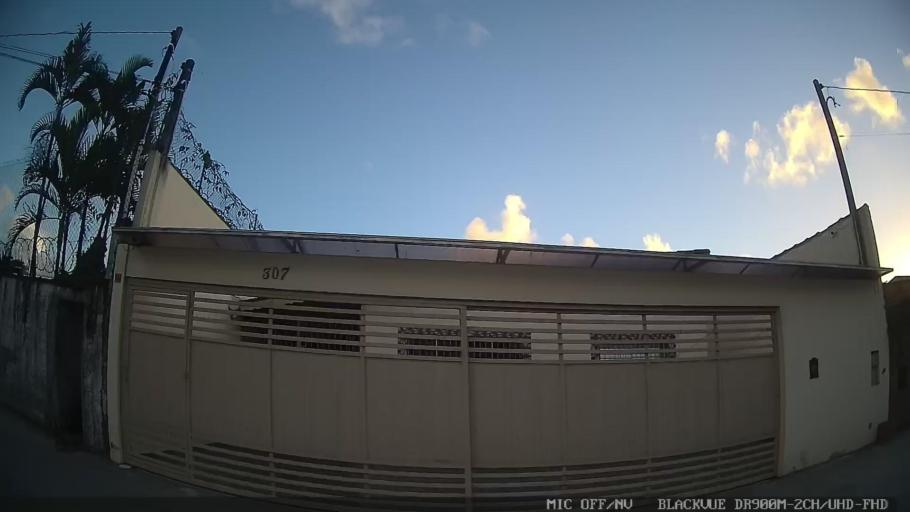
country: BR
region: Sao Paulo
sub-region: Itanhaem
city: Itanhaem
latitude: -24.1455
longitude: -46.7289
